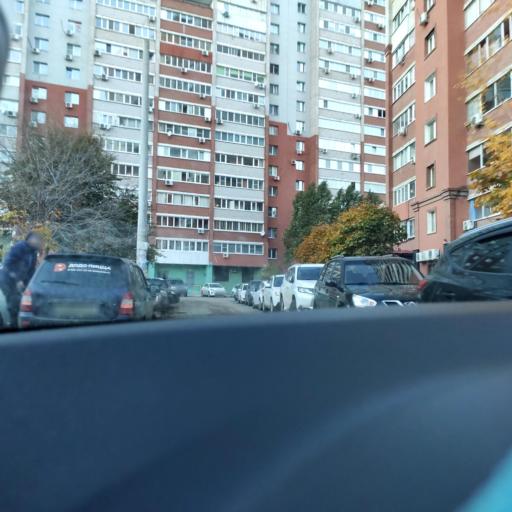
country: RU
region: Samara
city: Samara
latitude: 53.2194
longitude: 50.2462
